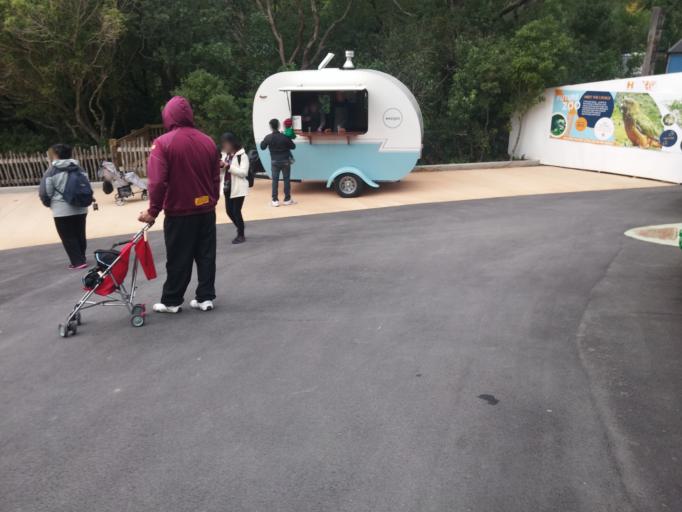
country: NZ
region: Wellington
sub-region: Wellington City
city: Brooklyn
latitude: -41.3208
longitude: 174.7851
